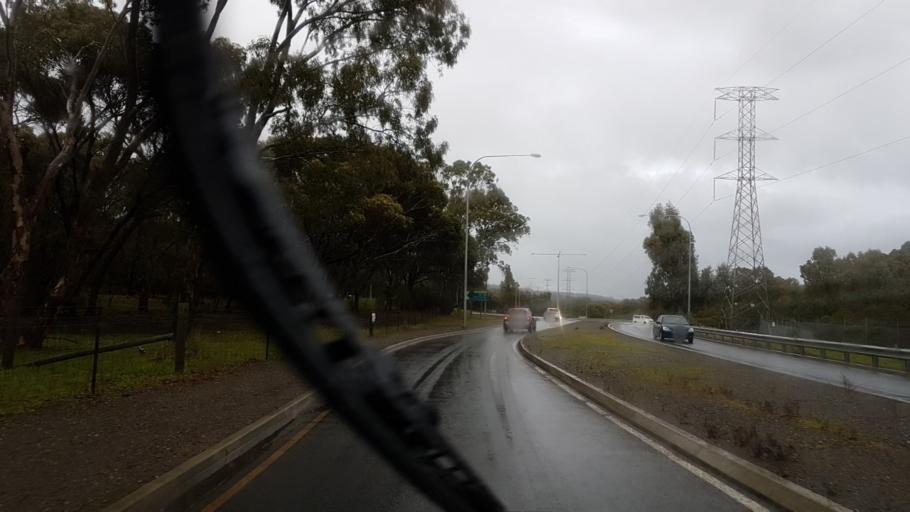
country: AU
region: South Australia
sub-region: Onkaparinga
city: Craigburn Farm
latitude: -35.0725
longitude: 138.5834
